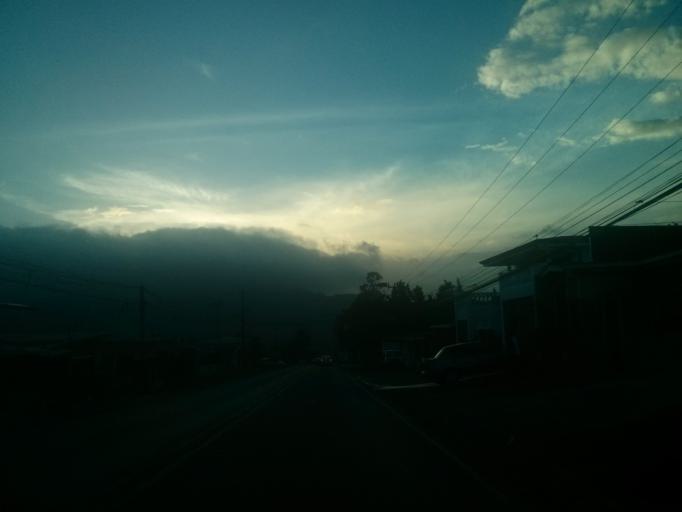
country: CR
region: Cartago
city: Cartago
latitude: 9.8781
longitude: -83.9289
